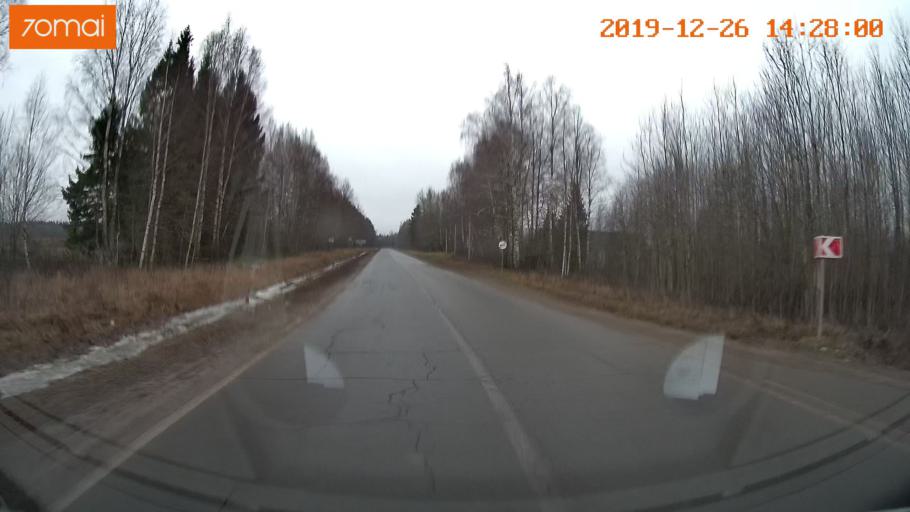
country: RU
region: Jaroslavl
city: Poshekhon'ye
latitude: 58.4803
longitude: 39.0584
